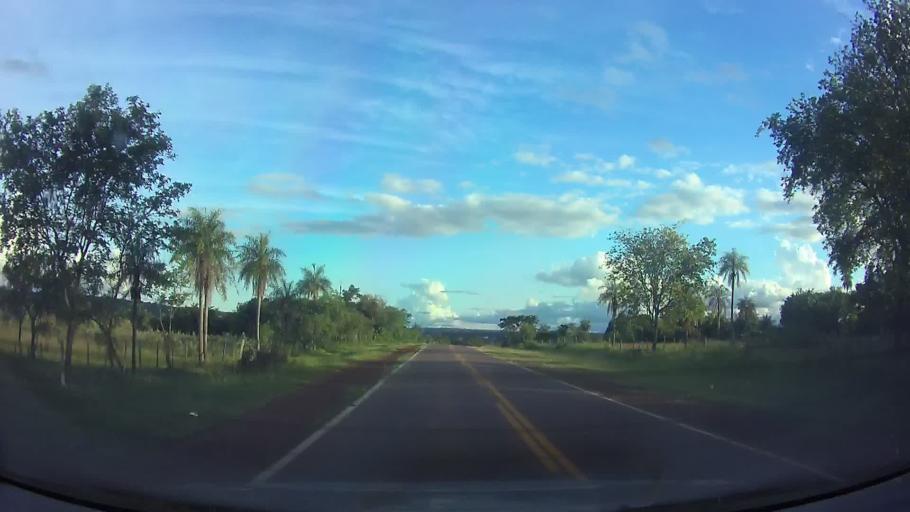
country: PY
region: Paraguari
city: Acahay
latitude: -25.8734
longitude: -57.1247
